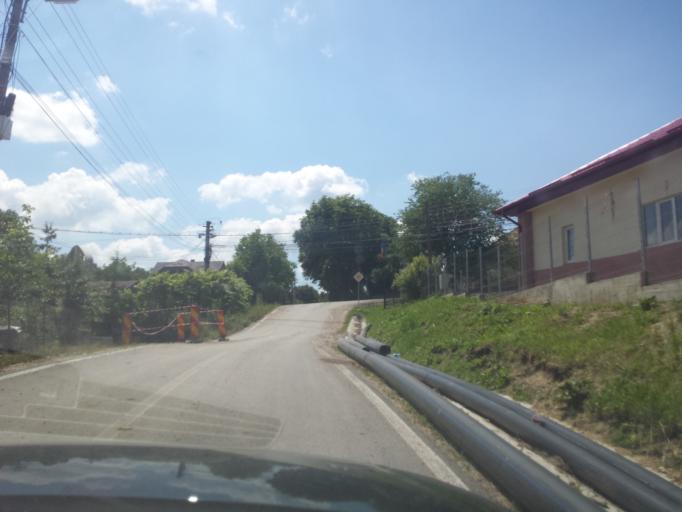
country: RO
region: Cluj
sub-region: Comuna Apahida
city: Dezmir
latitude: 46.7645
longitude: 23.7190
